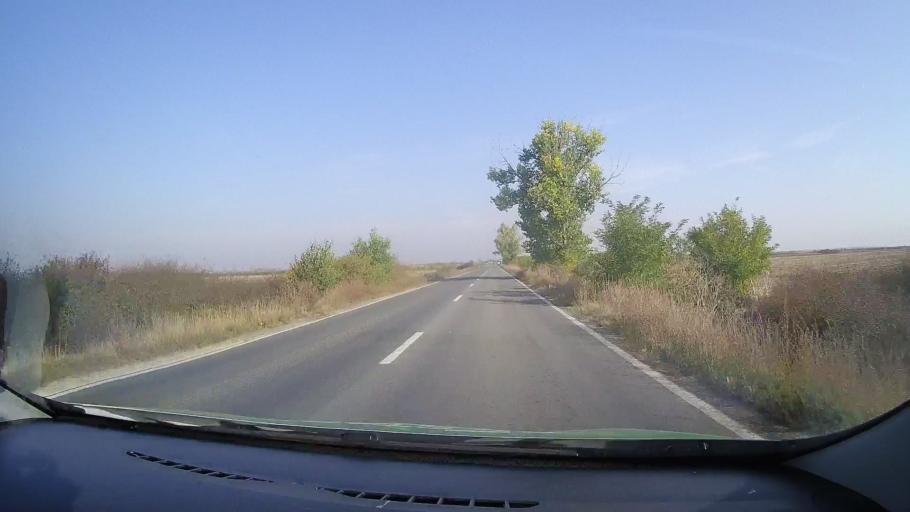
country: RO
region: Arad
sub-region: Comuna Pilu
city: Pilu
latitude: 46.6011
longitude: 21.3500
